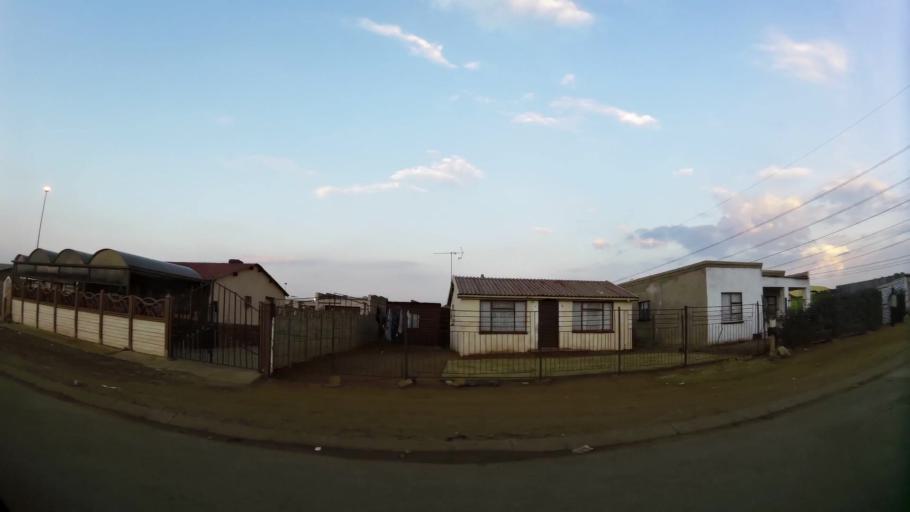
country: ZA
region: Gauteng
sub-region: City of Johannesburg Metropolitan Municipality
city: Orange Farm
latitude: -26.5581
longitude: 27.8618
